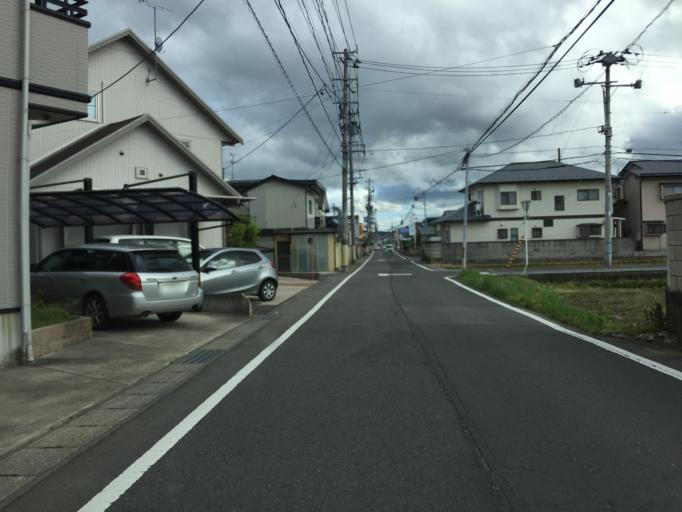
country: JP
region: Fukushima
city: Fukushima-shi
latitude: 37.7699
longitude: 140.4443
